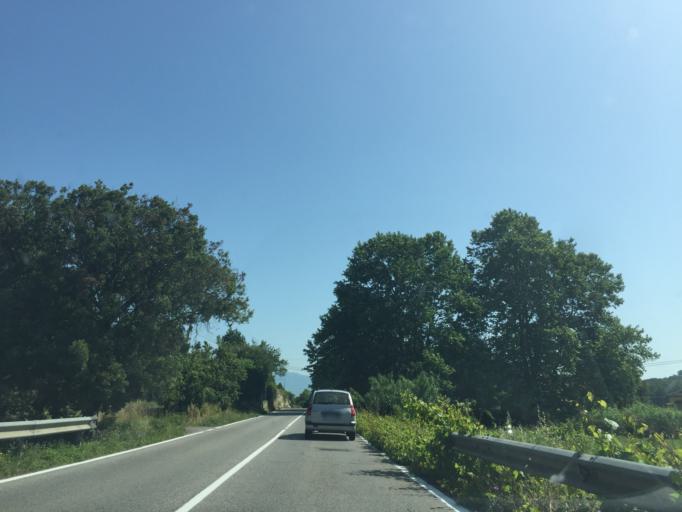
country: IT
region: Tuscany
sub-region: Province of Pisa
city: Asciano
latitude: 43.7963
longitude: 10.4812
